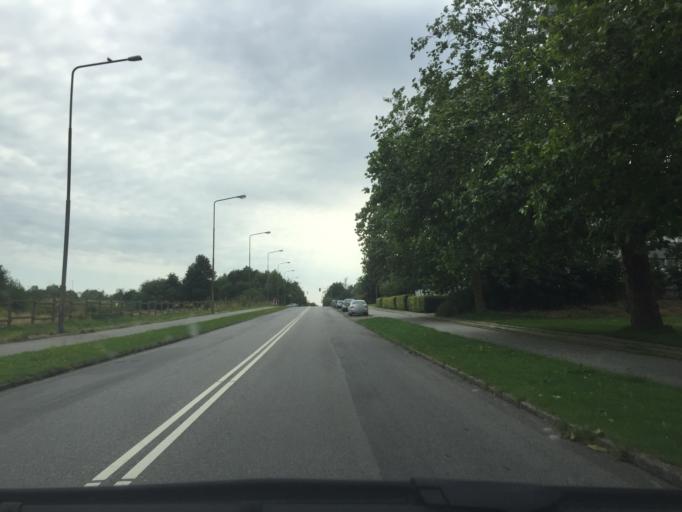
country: DK
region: Capital Region
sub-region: Lyngby-Tarbaek Kommune
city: Kongens Lyngby
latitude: 55.7972
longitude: 12.5299
